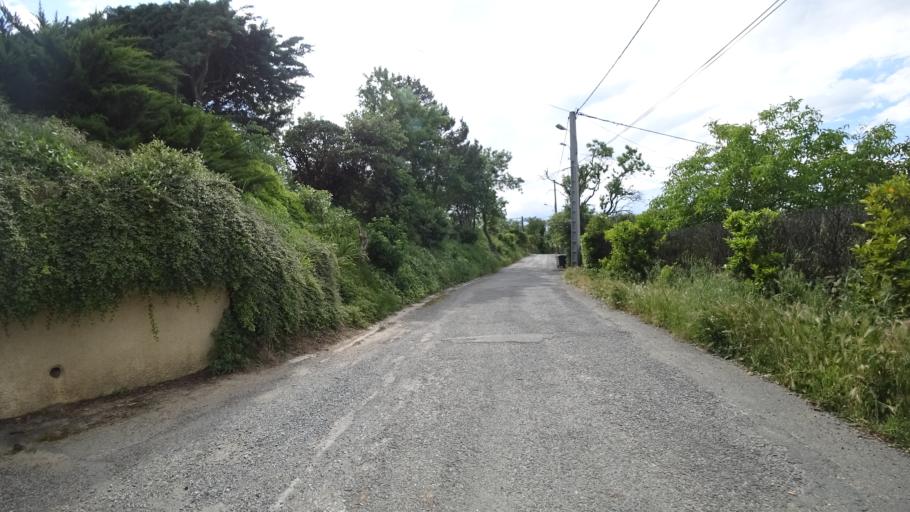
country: FR
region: Languedoc-Roussillon
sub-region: Departement de l'Aude
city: Ginestas
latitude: 43.2655
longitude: 2.8745
